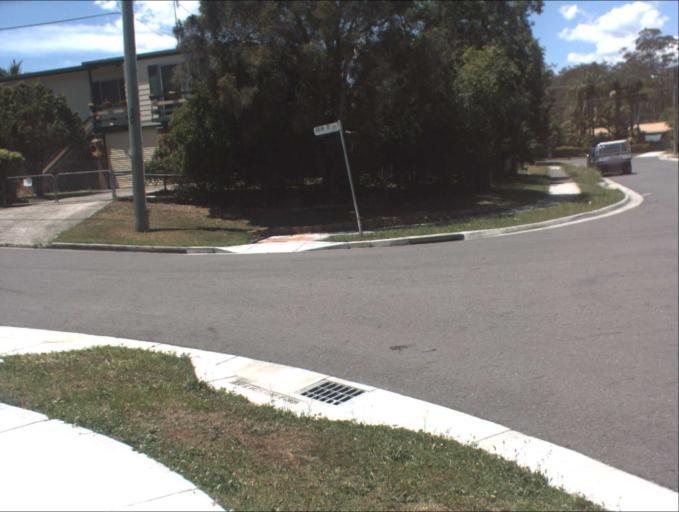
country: AU
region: Queensland
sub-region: Logan
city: Logan City
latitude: -27.6633
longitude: 153.1062
